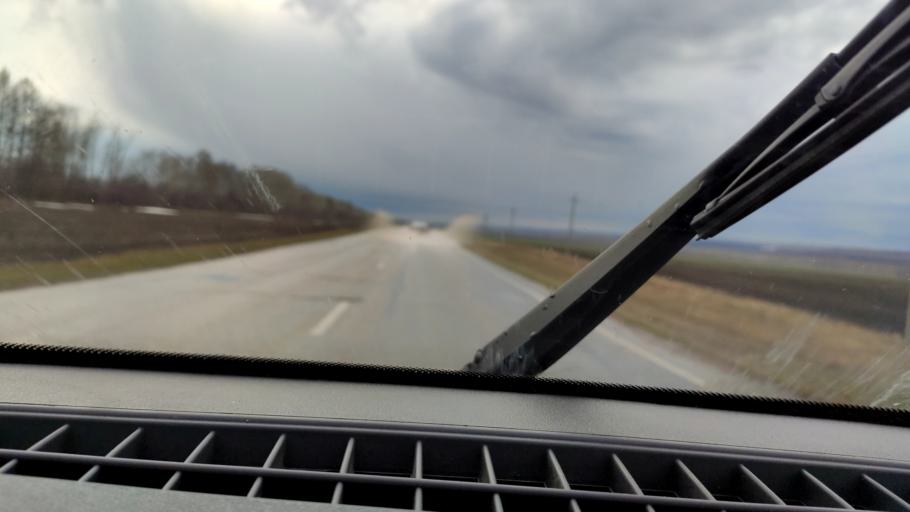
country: RU
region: Bashkortostan
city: Chekmagush
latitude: 55.1080
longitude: 54.9689
